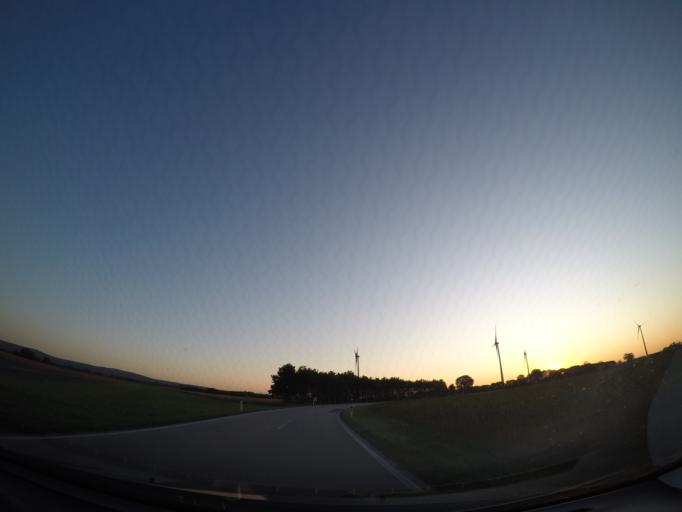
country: AT
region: Lower Austria
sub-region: Politischer Bezirk Baden
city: Seibersdorf
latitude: 47.9583
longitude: 16.5065
